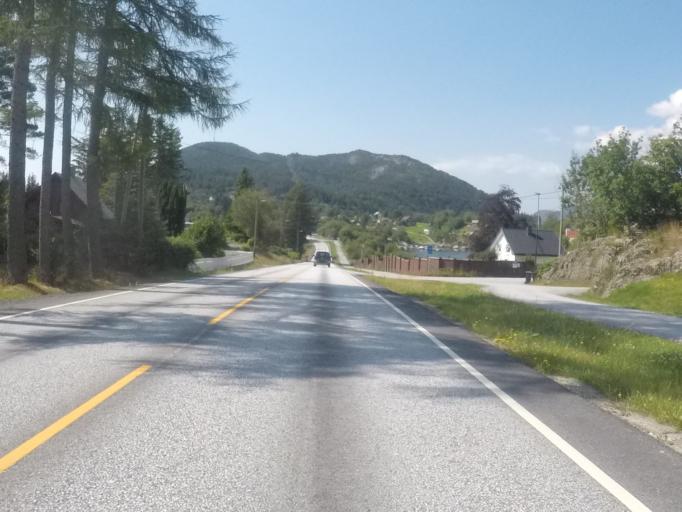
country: NO
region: Sogn og Fjordane
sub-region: Flora
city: Floro
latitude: 61.6020
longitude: 5.1461
